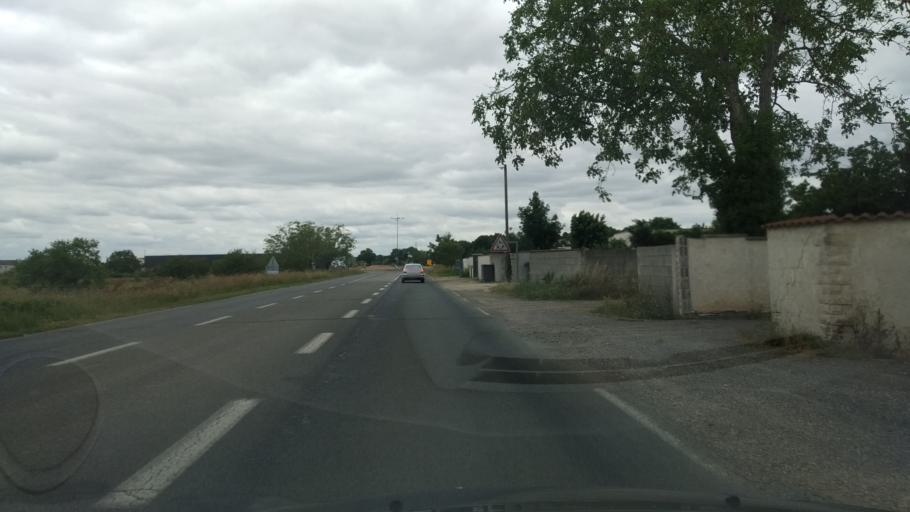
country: FR
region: Poitou-Charentes
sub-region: Departement de la Vienne
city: Migne-Auxances
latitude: 46.6039
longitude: 0.3102
